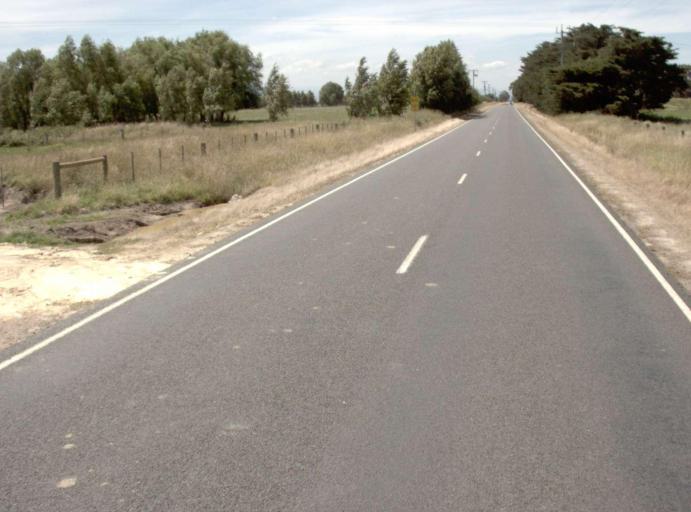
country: AU
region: Victoria
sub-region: Wellington
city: Heyfield
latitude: -38.0601
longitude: 146.8730
